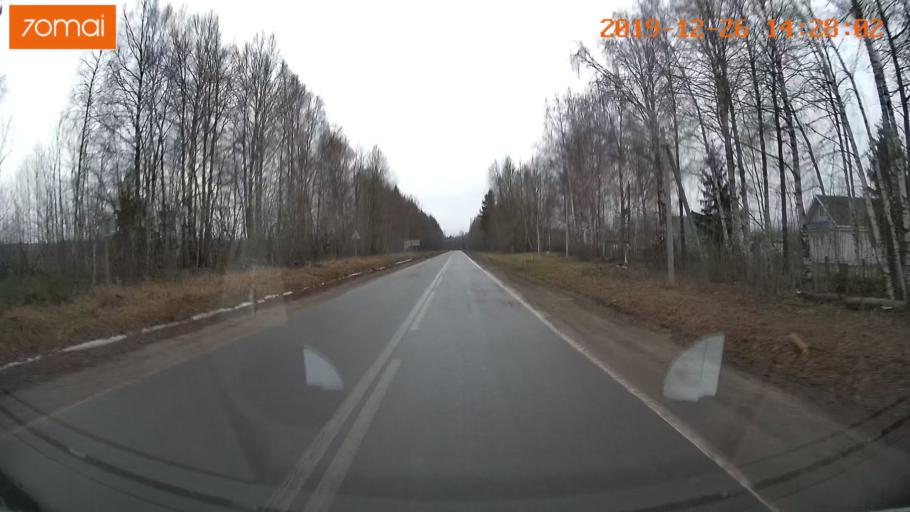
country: RU
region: Jaroslavl
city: Poshekhon'ye
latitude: 58.4799
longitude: 39.0578
